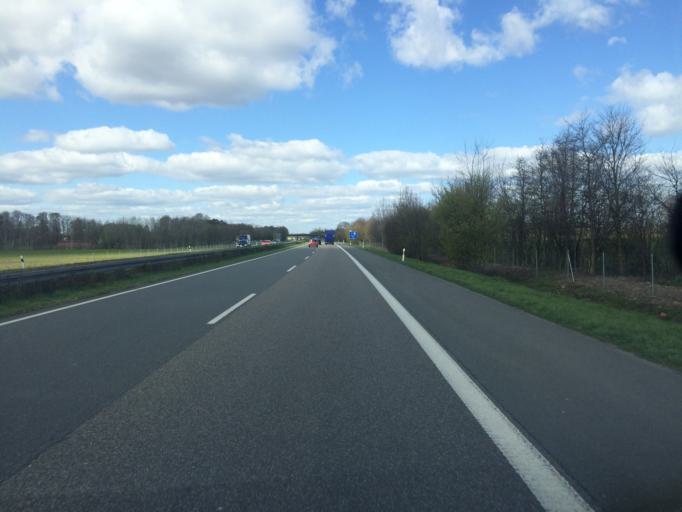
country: DE
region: North Rhine-Westphalia
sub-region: Regierungsbezirk Munster
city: Heek
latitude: 52.0940
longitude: 7.0849
